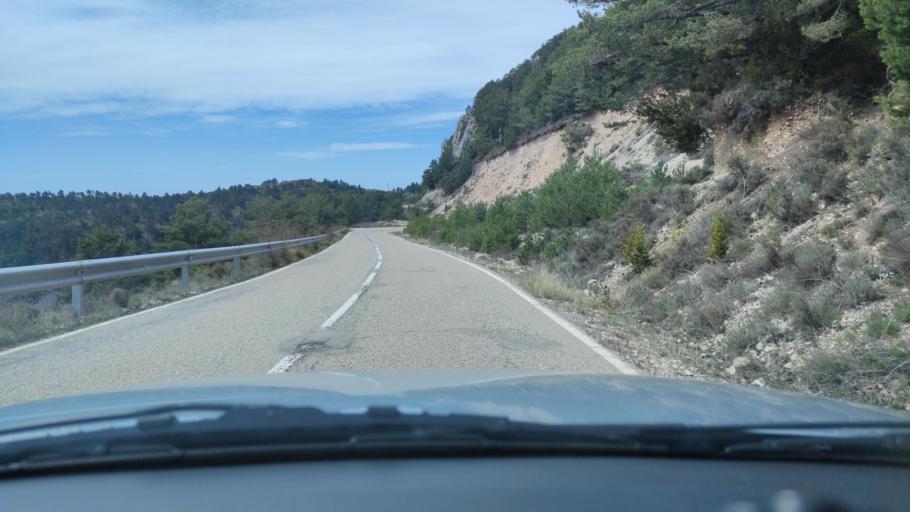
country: ES
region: Catalonia
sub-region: Provincia de Lleida
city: Olius
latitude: 42.1429
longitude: 1.5504
